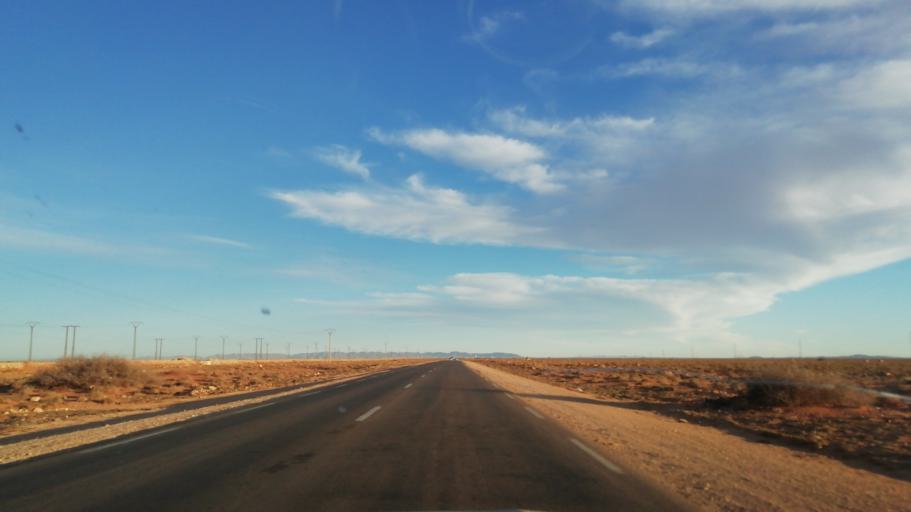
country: DZ
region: Wilaya de Naama
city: Naama
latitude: 33.7407
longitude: -0.7724
